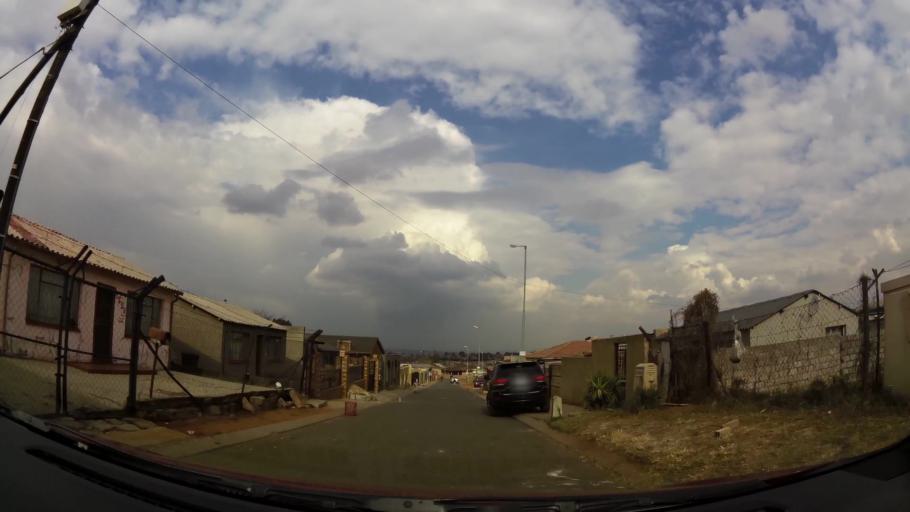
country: ZA
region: Gauteng
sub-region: City of Johannesburg Metropolitan Municipality
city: Soweto
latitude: -26.2346
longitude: 27.8711
